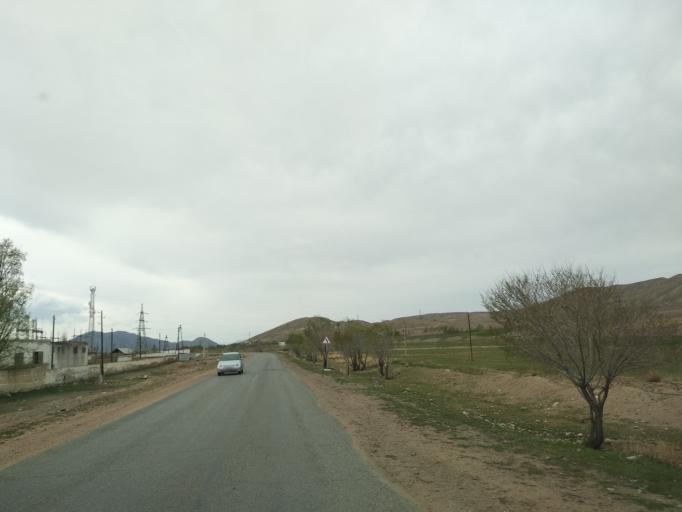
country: KG
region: Ysyk-Koel
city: Bokombayevskoye
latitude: 42.1257
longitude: 76.9961
